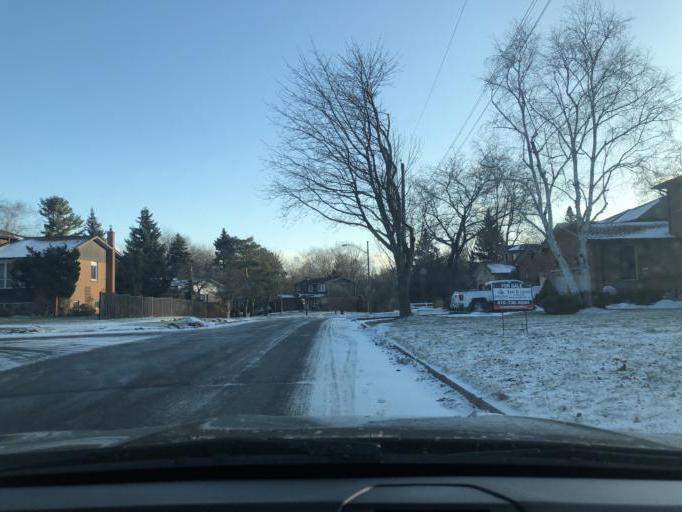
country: CA
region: Ontario
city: Scarborough
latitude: 43.7796
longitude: -79.1510
